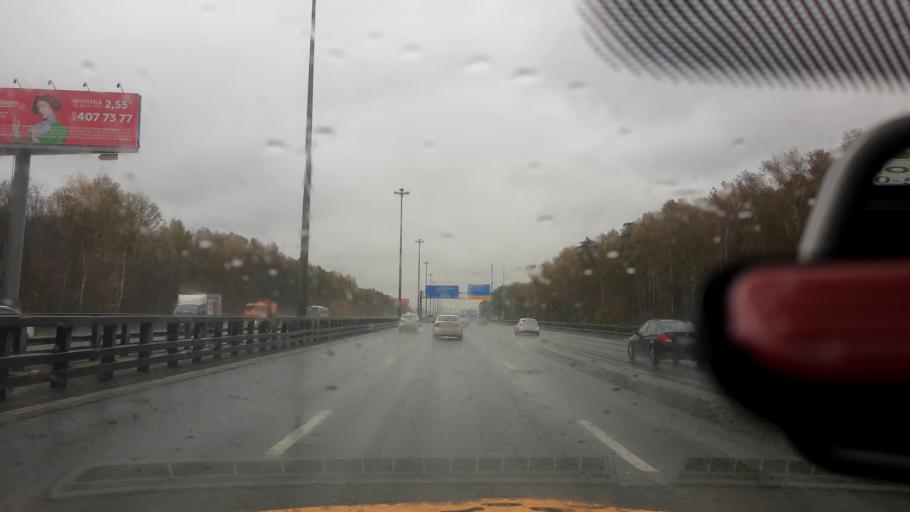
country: RU
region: Moscow
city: Solntsevo
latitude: 55.6206
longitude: 37.4022
